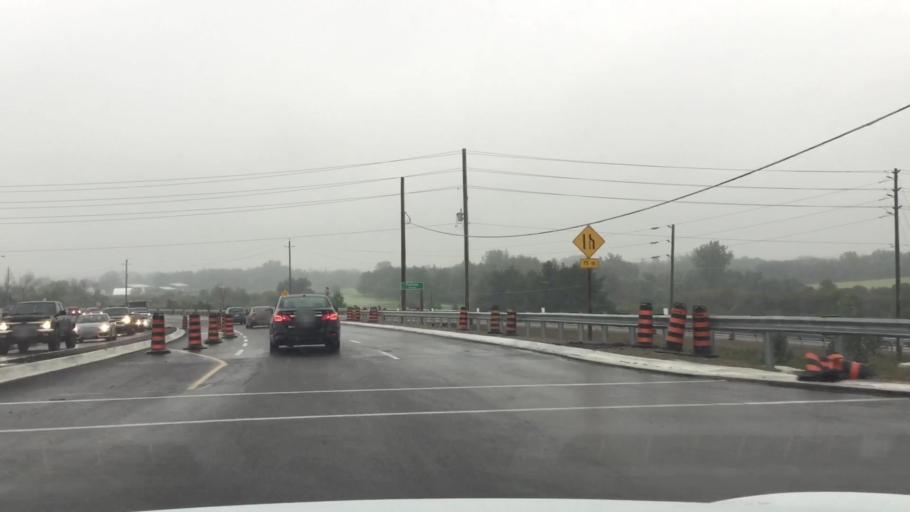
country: CA
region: Ontario
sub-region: Oxford County
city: Woodstock
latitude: 43.1087
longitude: -80.7357
